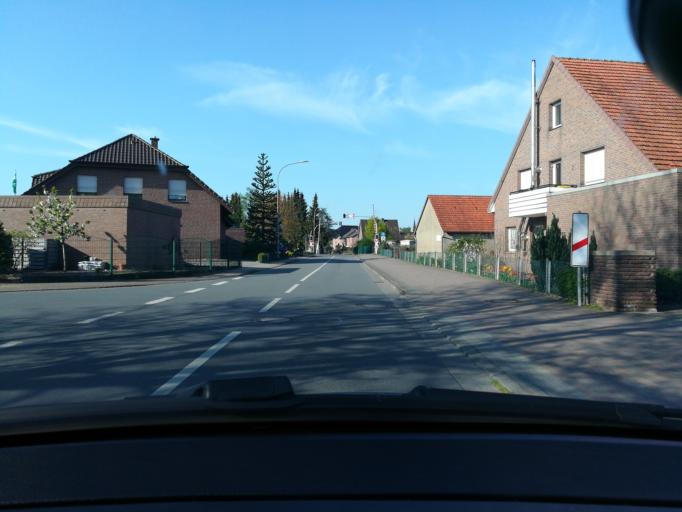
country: DE
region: North Rhine-Westphalia
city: Versmold
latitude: 52.0343
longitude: 8.1497
